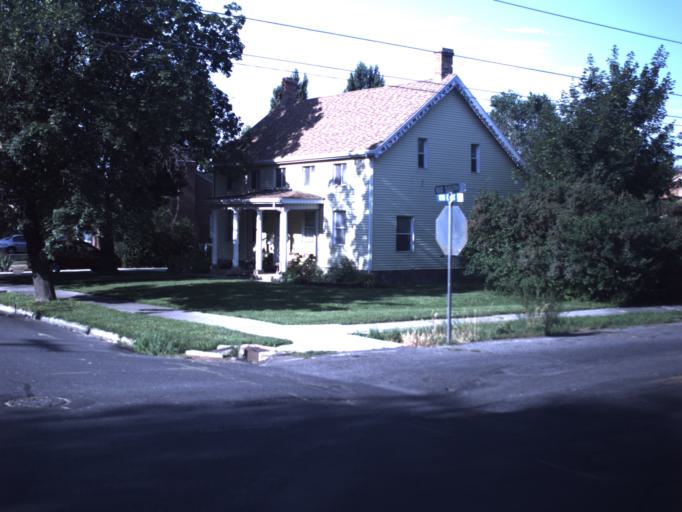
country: US
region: Utah
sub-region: Utah County
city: American Fork
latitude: 40.3748
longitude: -111.7960
